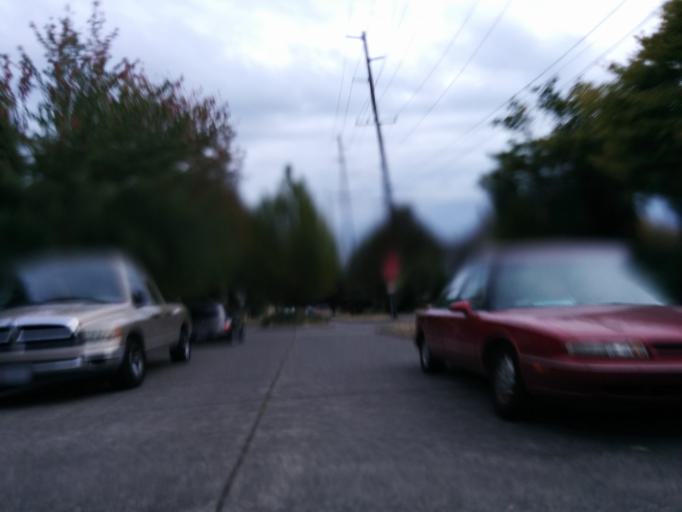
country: US
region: Washington
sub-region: King County
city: Seattle
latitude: 47.6713
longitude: -122.3686
